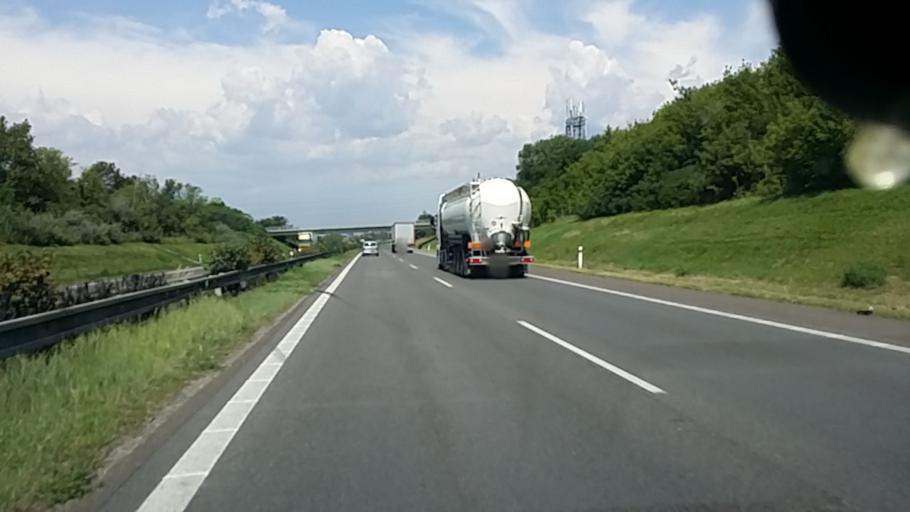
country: SK
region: Bratislavsky
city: Stupava
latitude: 48.2849
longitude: 17.0098
